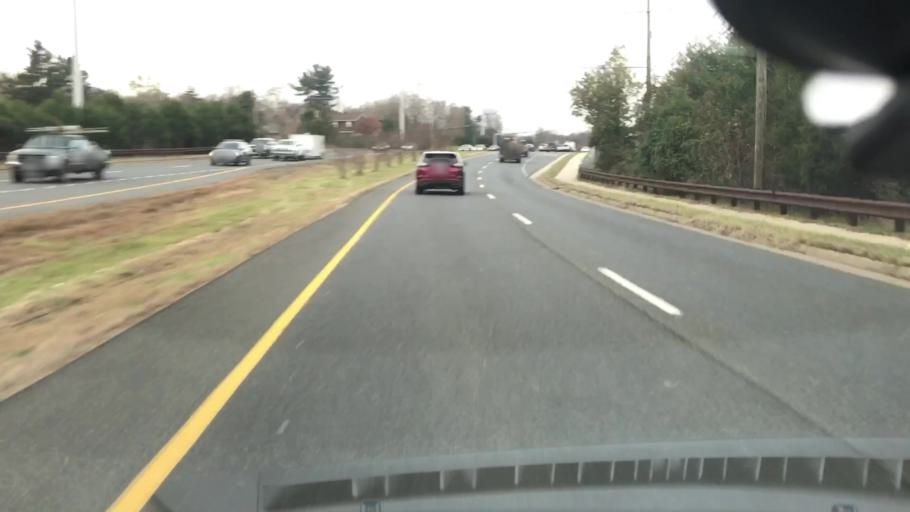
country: US
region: Virginia
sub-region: City of Fairfax
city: Fairfax
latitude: 38.8300
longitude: -77.3250
